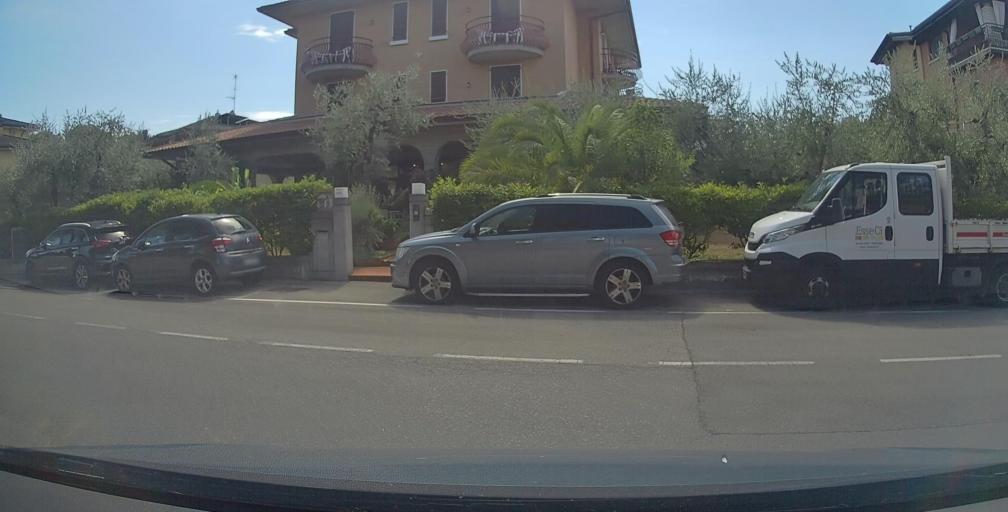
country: IT
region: Lombardy
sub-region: Provincia di Brescia
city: Sirmione
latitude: 45.4678
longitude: 10.6059
